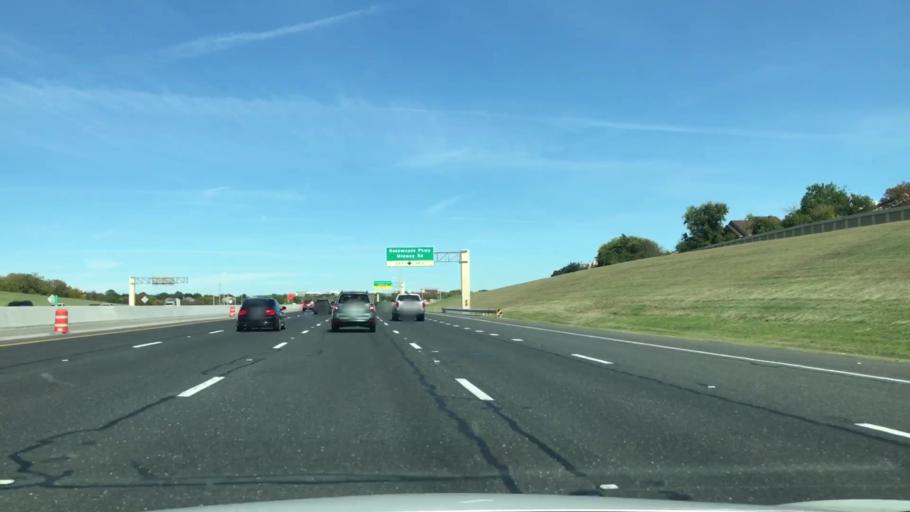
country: US
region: Texas
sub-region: Dallas County
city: Addison
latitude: 33.0060
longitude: -96.8530
